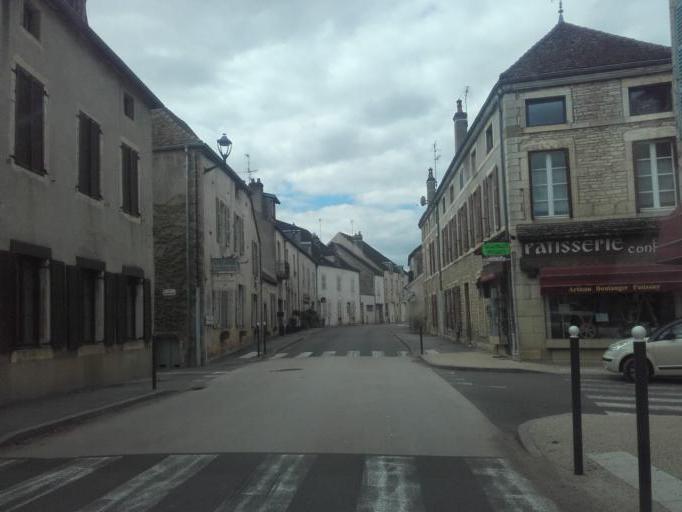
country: FR
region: Bourgogne
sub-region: Departement de la Cote-d'Or
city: Bligny-les-Beaune
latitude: 47.0079
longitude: 4.7967
